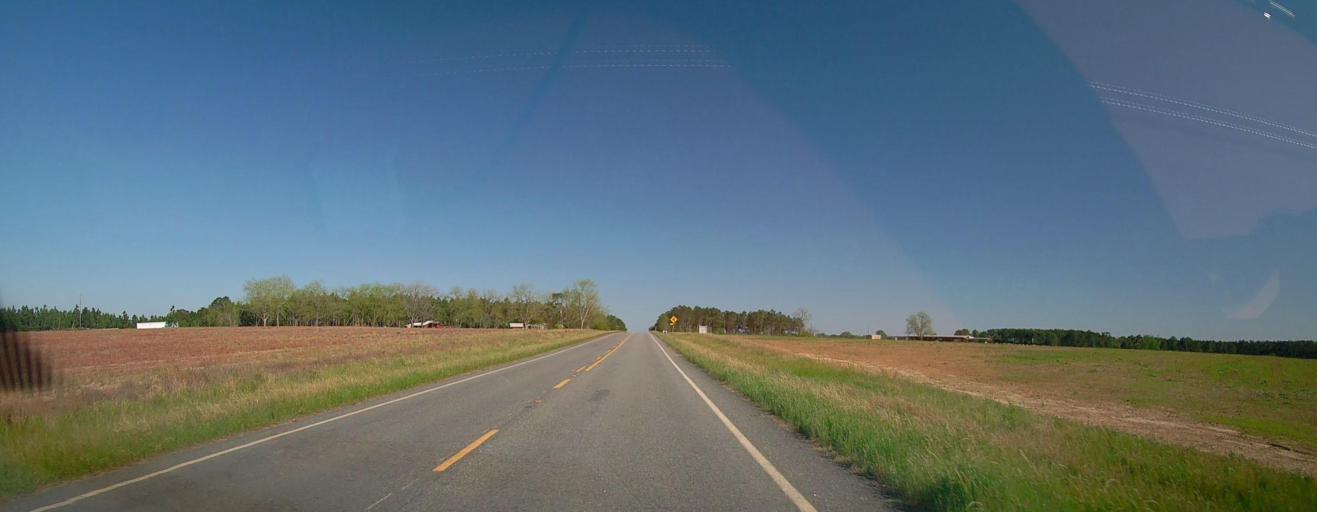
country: US
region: Georgia
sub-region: Wilcox County
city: Rochelle
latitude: 31.9914
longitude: -83.4684
